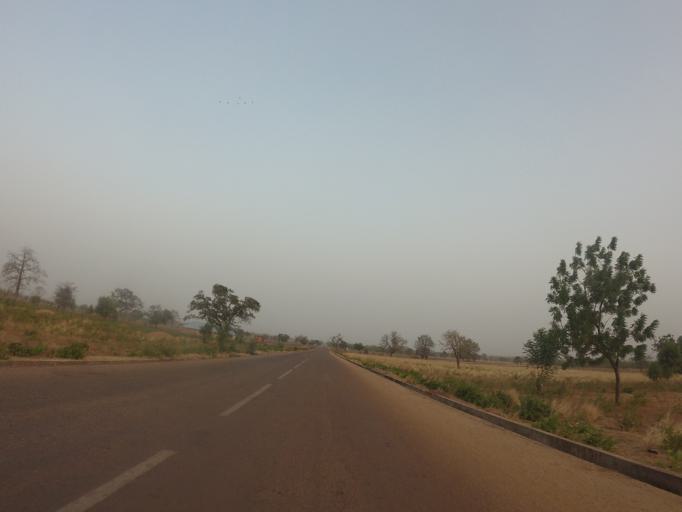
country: GH
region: Northern
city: Tamale
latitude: 9.4436
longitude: -1.1113
